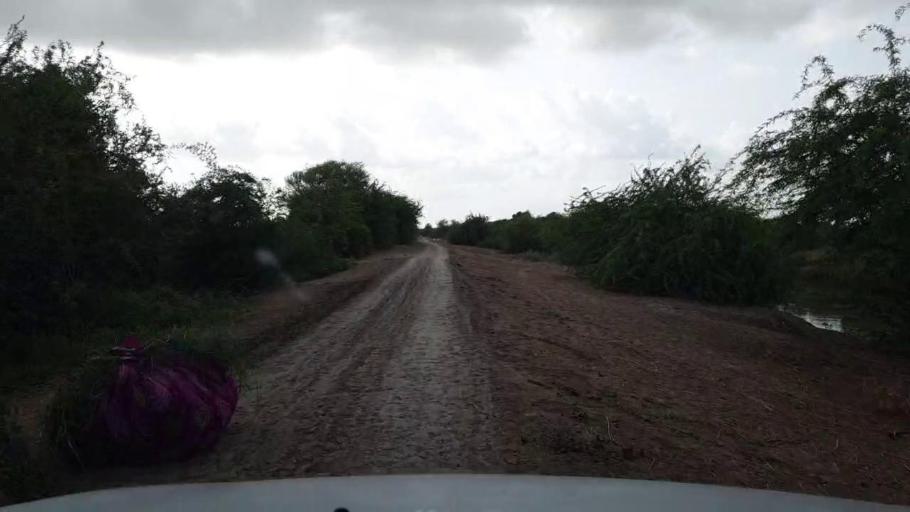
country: PK
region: Sindh
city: Kario
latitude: 24.7517
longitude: 68.6138
